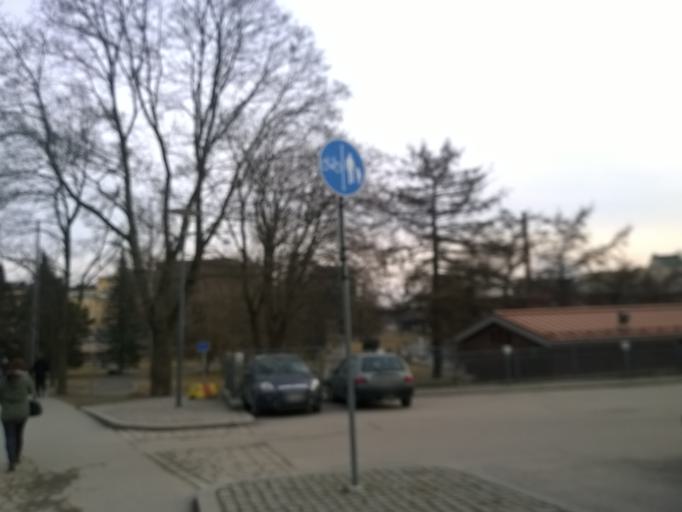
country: FI
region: Pirkanmaa
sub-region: Tampere
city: Tampere
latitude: 61.5007
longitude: 23.7642
